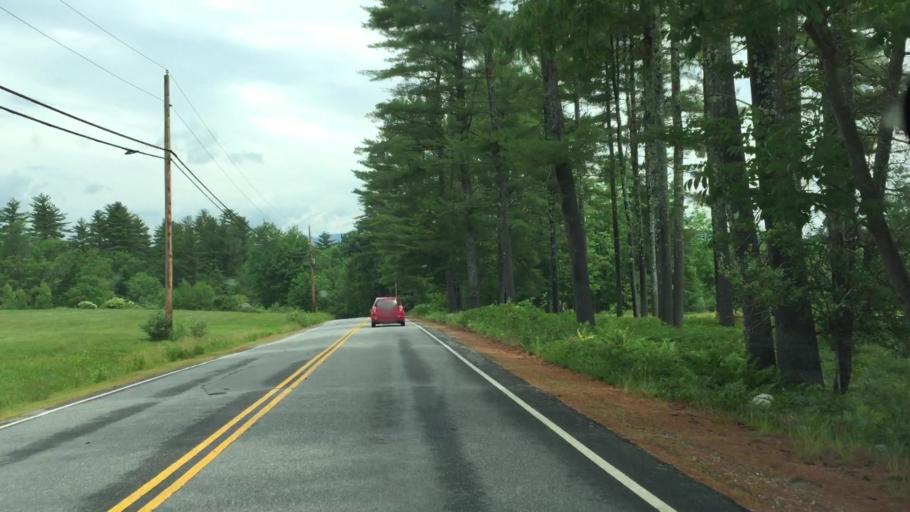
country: US
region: New Hampshire
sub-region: Carroll County
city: Sandwich
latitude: 43.7999
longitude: -71.4430
